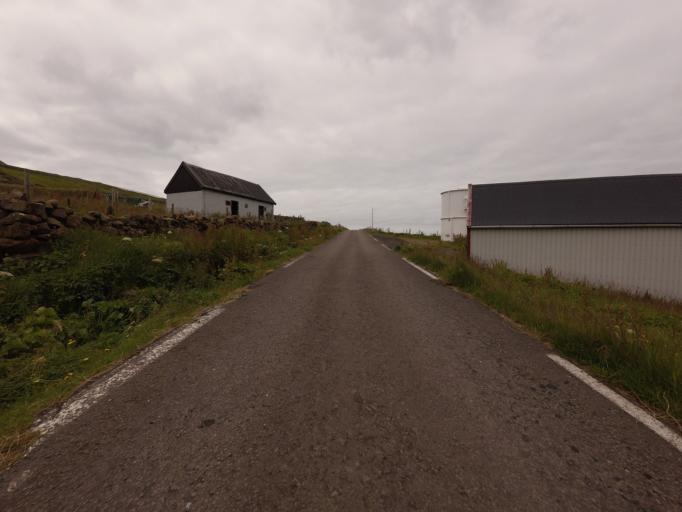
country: FO
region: Suduroy
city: Tvoroyri
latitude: 61.5205
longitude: -6.8833
